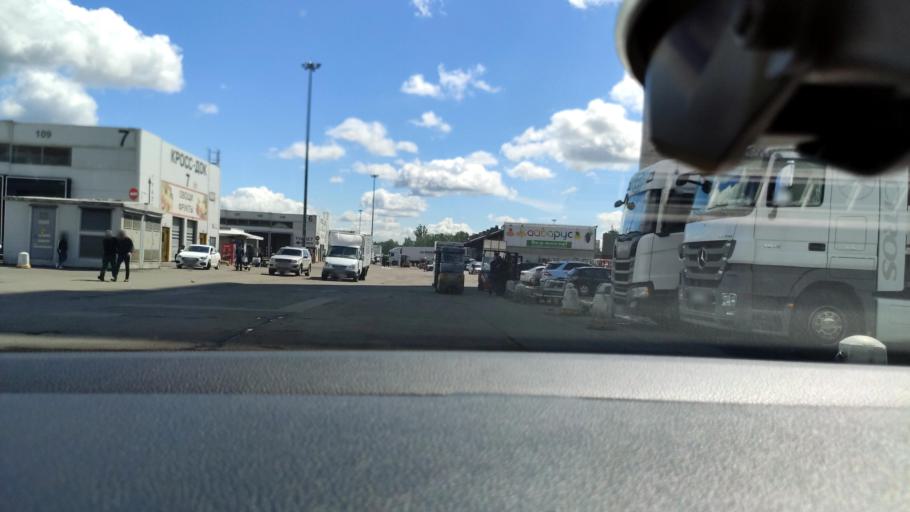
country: RU
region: Moskovskaya
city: Mosrentgen
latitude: 55.5979
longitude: 37.4631
